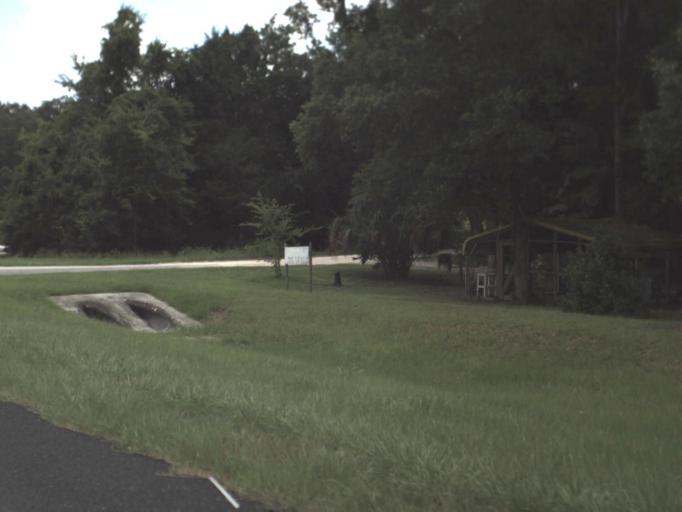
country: US
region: Florida
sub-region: Levy County
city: Williston
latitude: 29.4009
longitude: -82.5071
